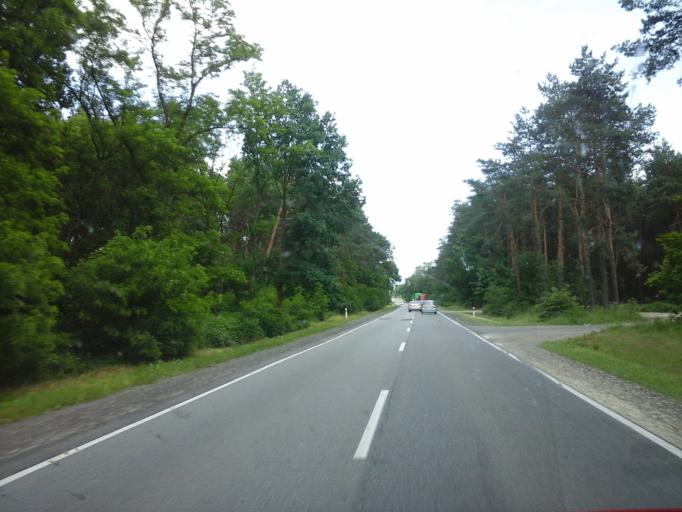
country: PL
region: Lodz Voivodeship
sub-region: Powiat opoczynski
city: Paradyz
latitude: 51.3105
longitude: 20.0898
